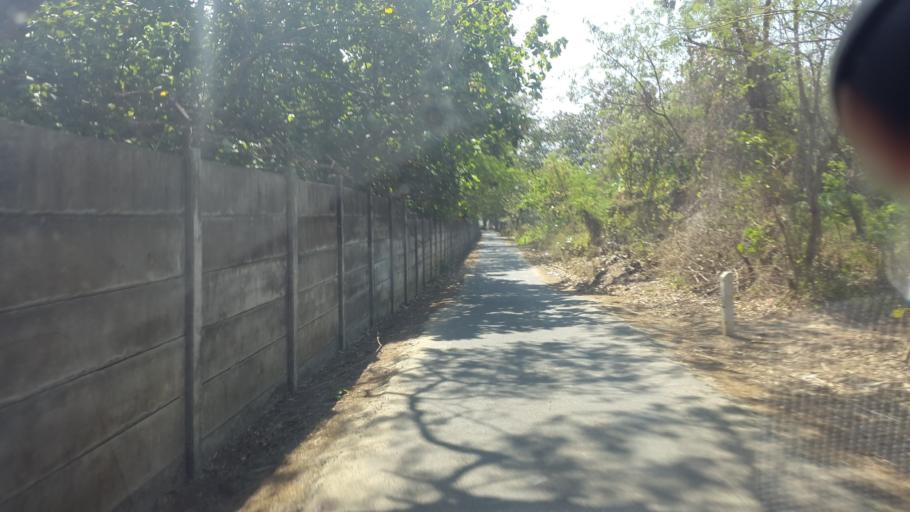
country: ID
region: West Java
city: Gunungbatu
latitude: -7.3315
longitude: 106.3990
